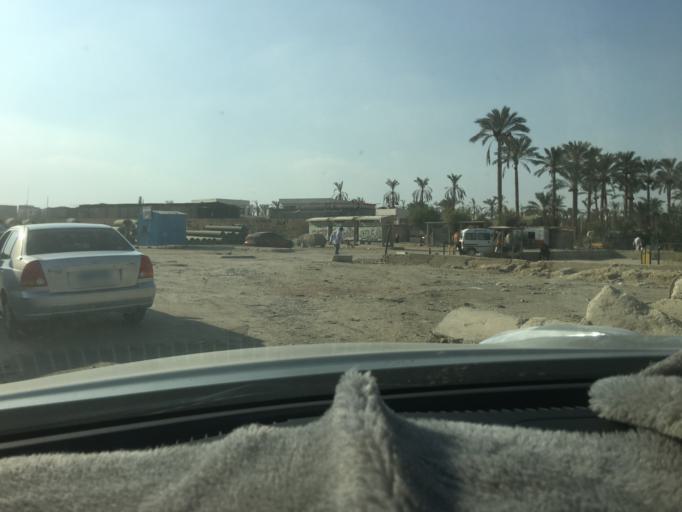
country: EG
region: Muhafazat al Qalyubiyah
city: Al Khankah
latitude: 30.1663
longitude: 31.3834
